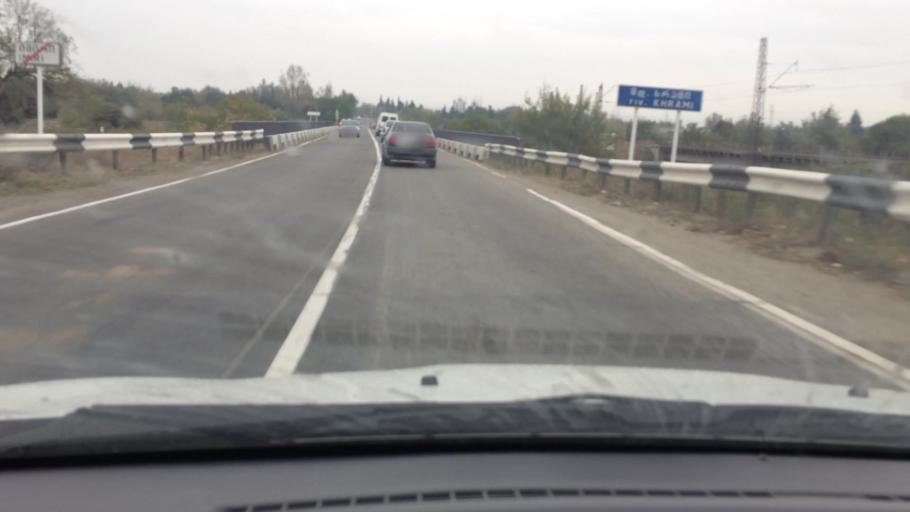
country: GE
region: Kvemo Kartli
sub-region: Marneuli
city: Marneuli
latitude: 41.4041
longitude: 44.8305
